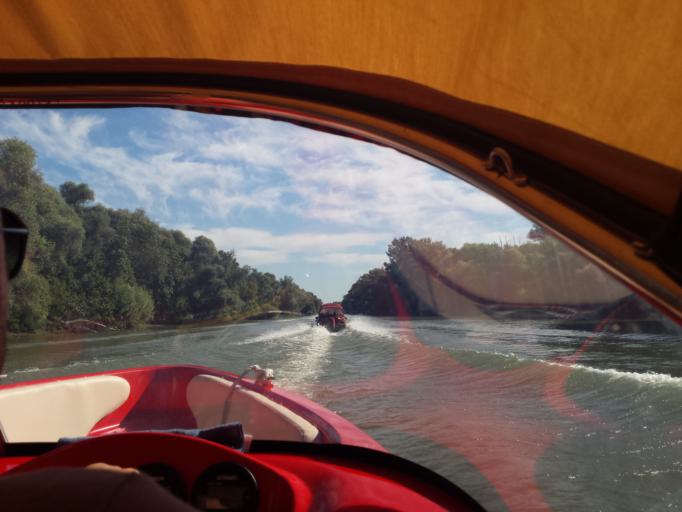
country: RO
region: Tulcea
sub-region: Comuna Nufaru
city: Malcoci
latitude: 45.2146
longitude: 28.8674
